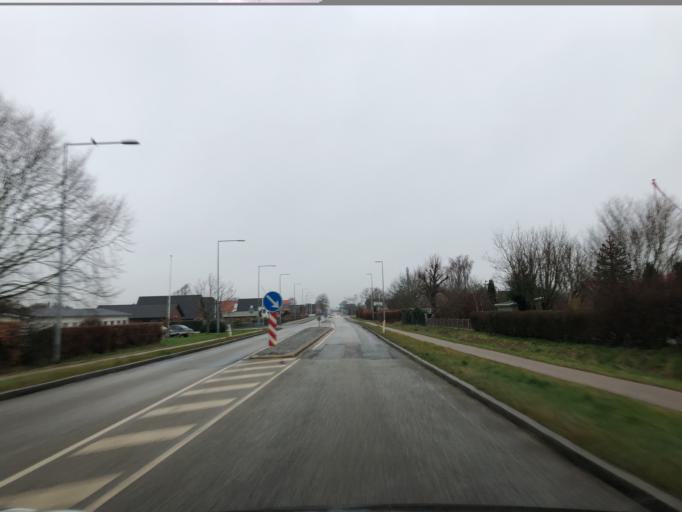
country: DK
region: Central Jutland
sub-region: Herning Kommune
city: Lind
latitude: 56.1013
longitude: 8.9798
